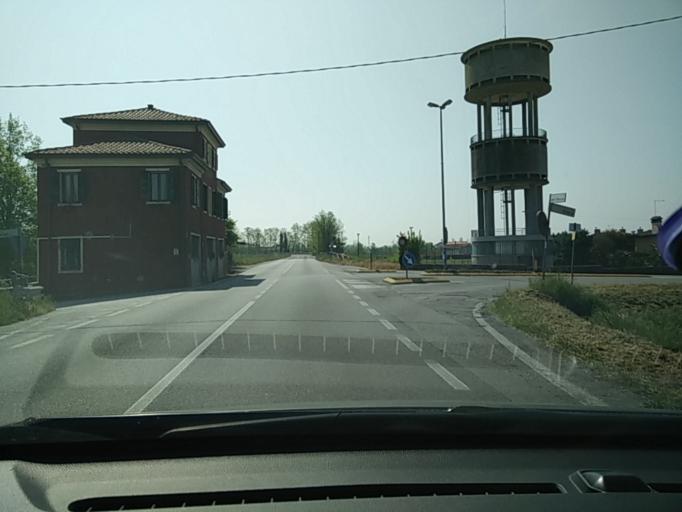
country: IT
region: Veneto
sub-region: Provincia di Venezia
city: Fossalta di Piave
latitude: 45.6348
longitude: 12.5244
